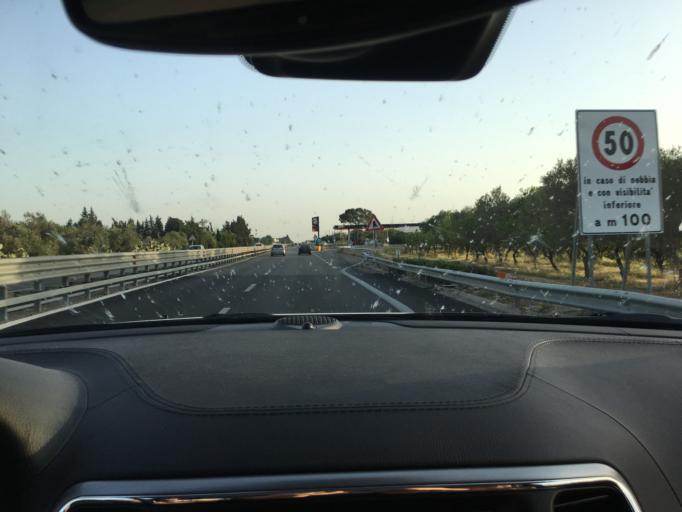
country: IT
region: Apulia
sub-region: Provincia di Lecce
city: Lequile
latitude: 40.2888
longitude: 18.1324
